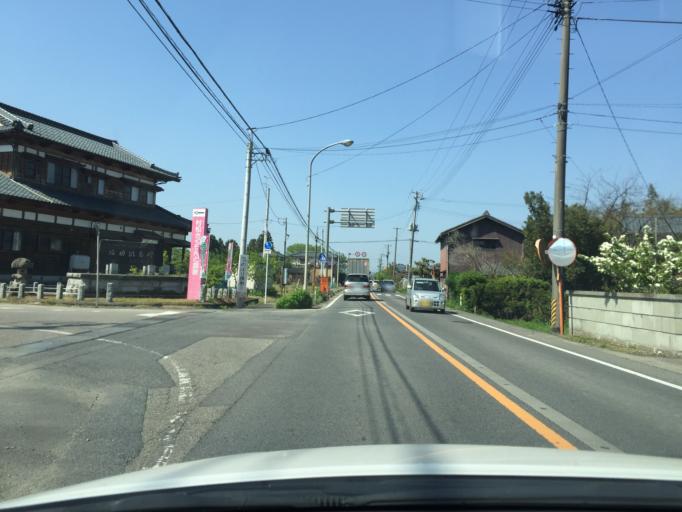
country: JP
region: Niigata
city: Muramatsu
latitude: 37.7075
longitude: 139.2023
